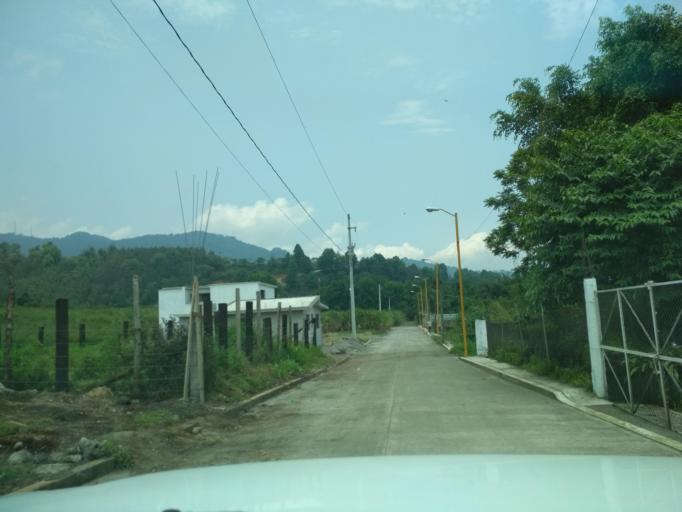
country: MX
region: Veracruz
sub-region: Mariano Escobedo
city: Mariano Escobedo
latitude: 18.9099
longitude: -97.1266
